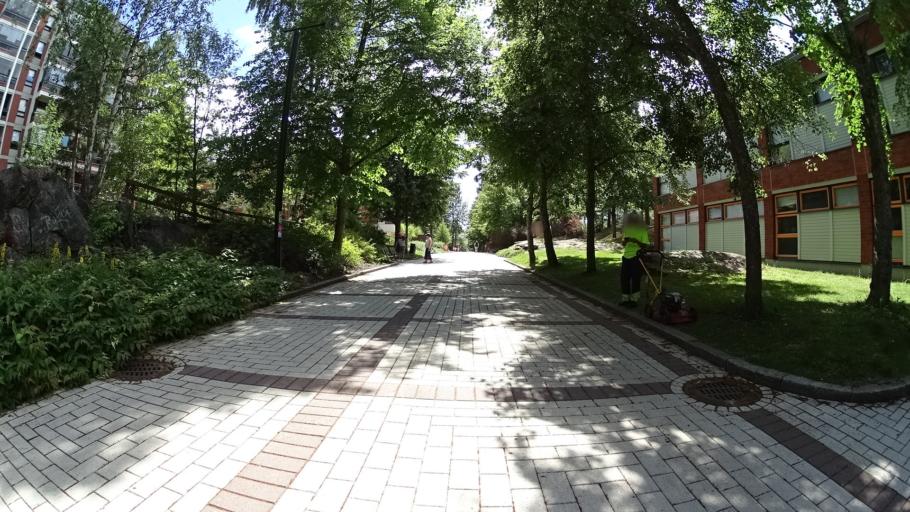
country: FI
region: Uusimaa
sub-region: Helsinki
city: Teekkarikylae
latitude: 60.2693
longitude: 24.8517
